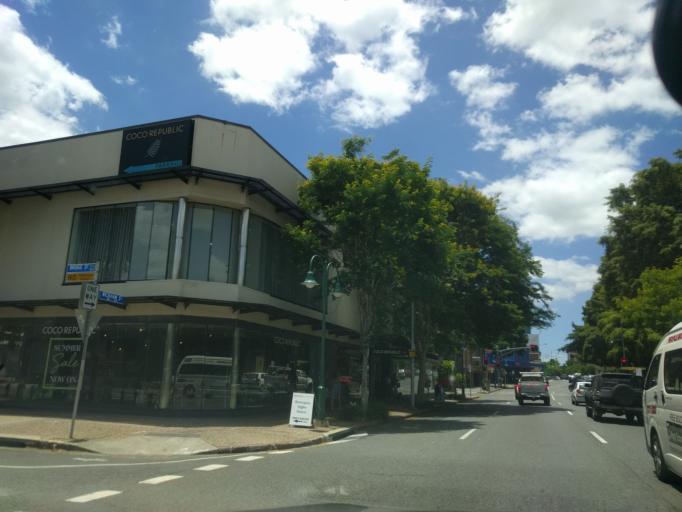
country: AU
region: Queensland
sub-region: Brisbane
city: Fortitude Valley
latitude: -27.4549
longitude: 153.0363
